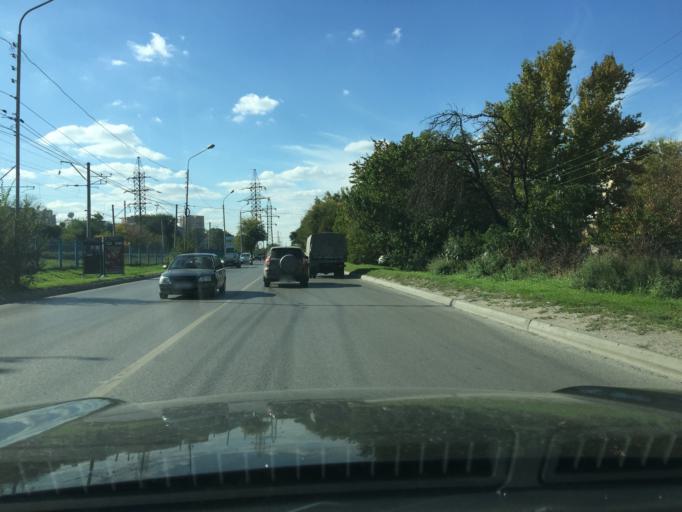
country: RU
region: Rostov
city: Rostov-na-Donu
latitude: 47.2447
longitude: 39.7166
